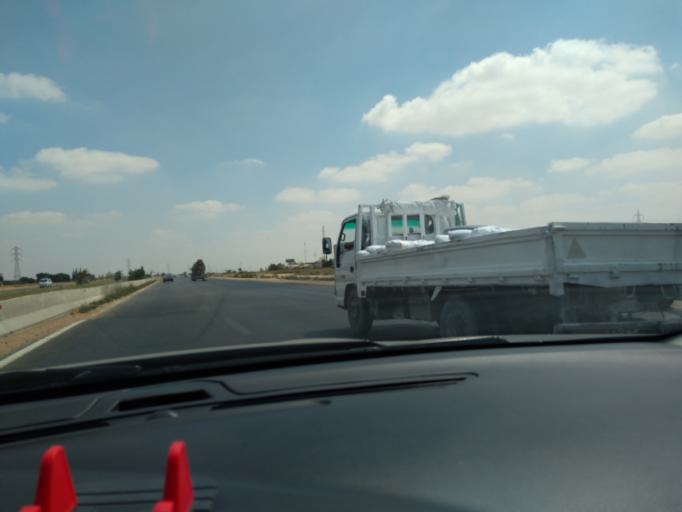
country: EG
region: Al Isma'iliyah
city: At Tall al Kabir
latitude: 30.3401
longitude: 31.8651
